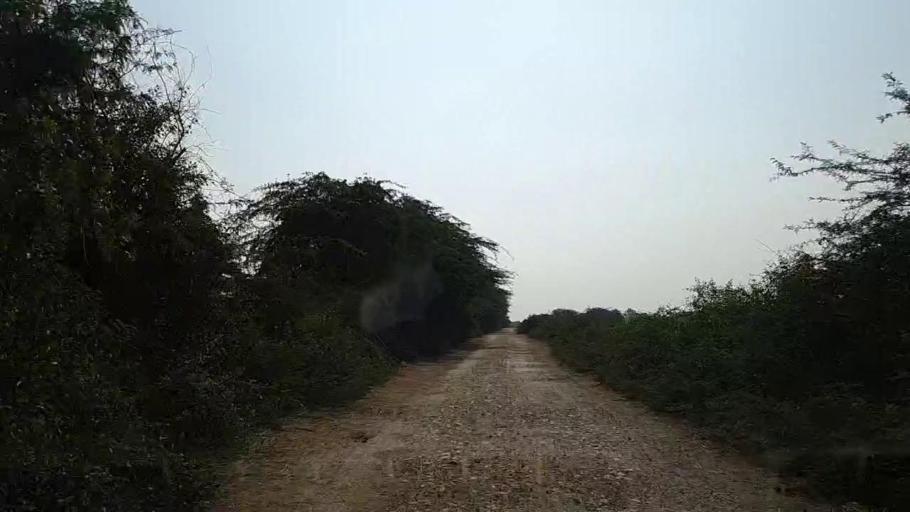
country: PK
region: Sindh
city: Mirpur Sakro
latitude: 24.6330
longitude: 67.6584
